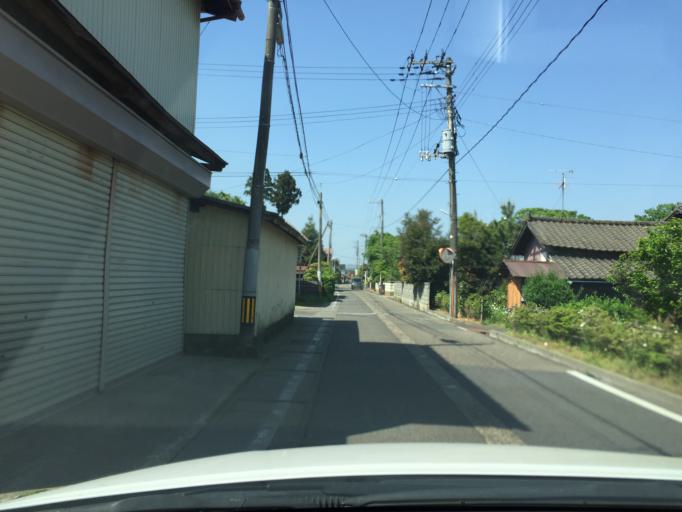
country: JP
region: Niigata
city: Muramatsu
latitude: 37.6976
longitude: 139.1848
